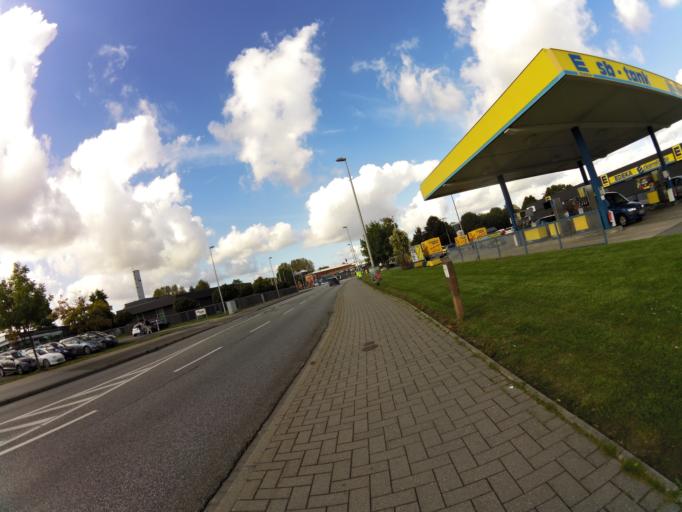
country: DE
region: Schleswig-Holstein
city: Eckernforde
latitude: 54.4505
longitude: 9.8329
